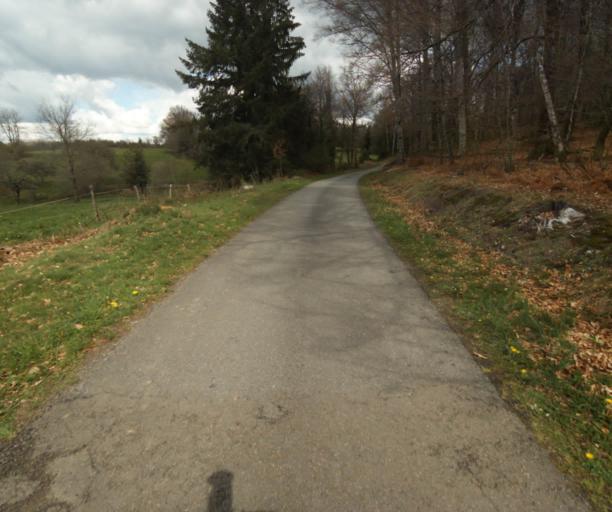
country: FR
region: Limousin
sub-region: Departement de la Correze
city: Correze
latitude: 45.2582
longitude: 1.9022
